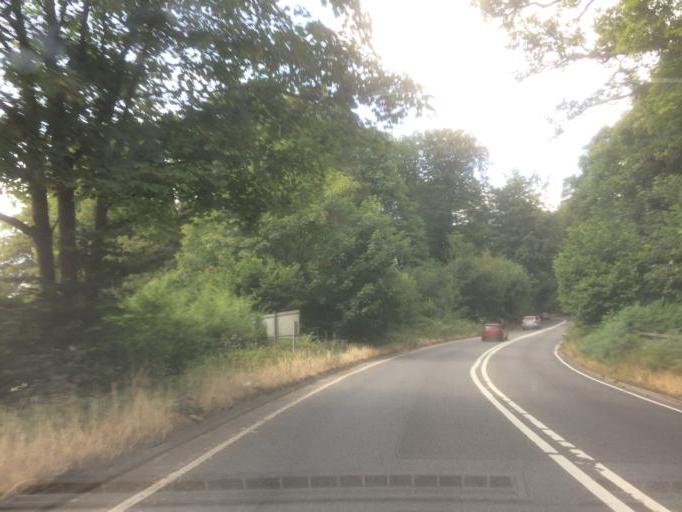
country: GB
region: England
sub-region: Buckinghamshire
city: Beaconsfield
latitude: 51.5800
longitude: -0.6278
